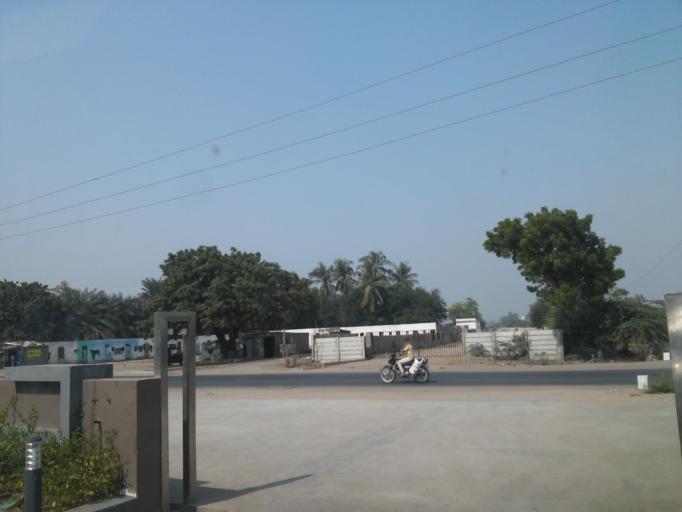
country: IN
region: Gujarat
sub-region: Kachchh
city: Mundra
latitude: 22.8375
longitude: 69.6999
